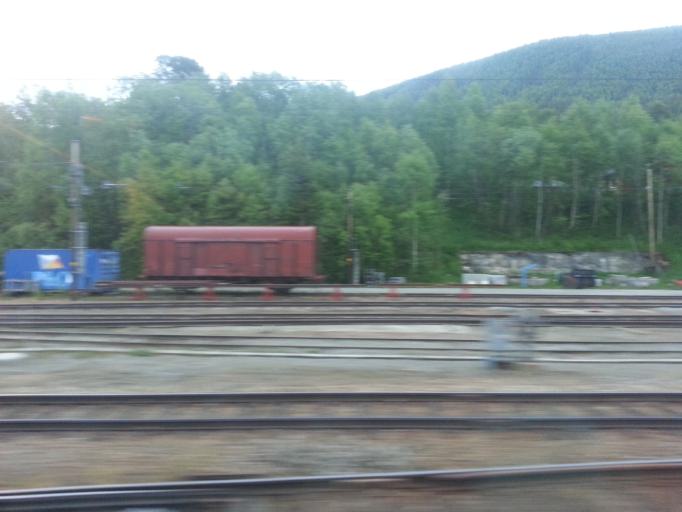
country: NO
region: Oppland
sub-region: Dovre
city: Dombas
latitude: 62.0692
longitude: 9.1262
